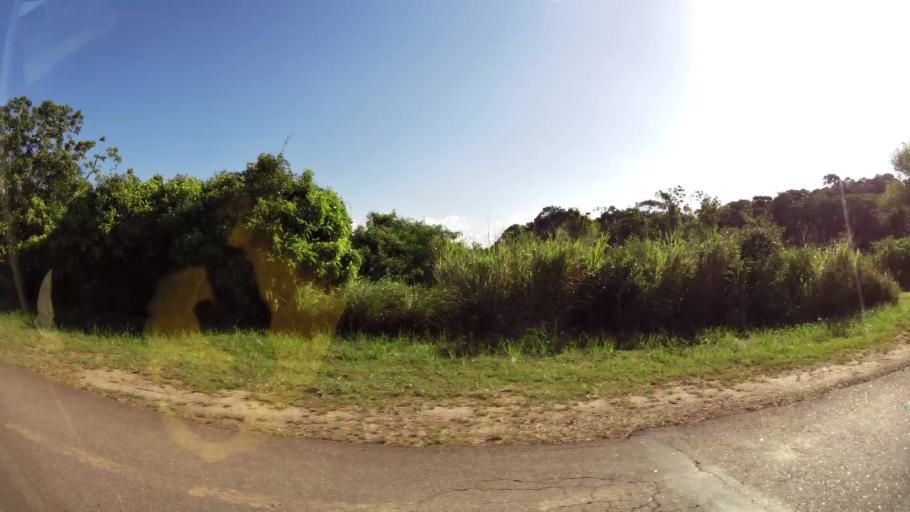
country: GF
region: Guyane
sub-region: Guyane
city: Matoury
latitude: 4.8608
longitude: -52.2761
